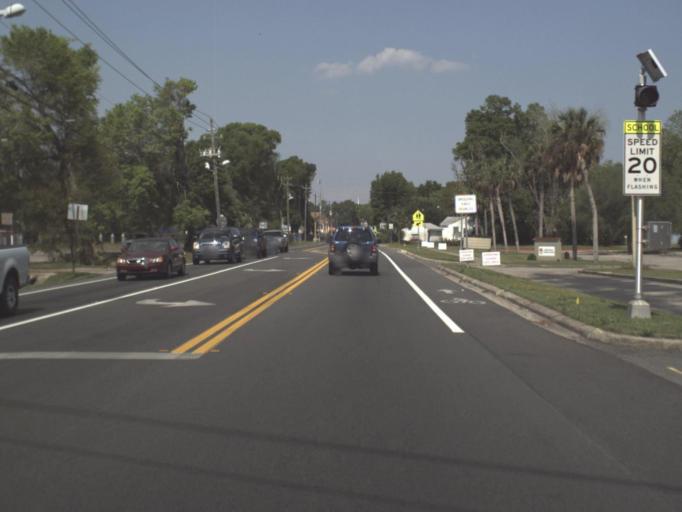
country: US
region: Florida
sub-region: Escambia County
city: Myrtle Grove
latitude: 30.4226
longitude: -87.3002
